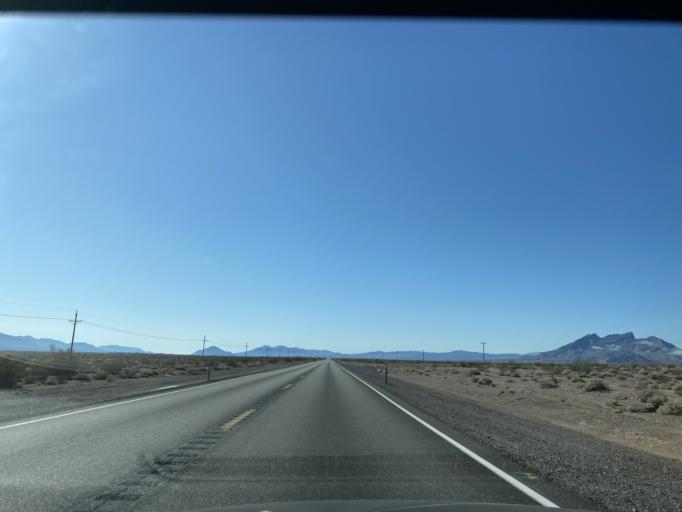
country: US
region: Nevada
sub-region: Nye County
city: Pahrump
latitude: 36.4652
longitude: -116.4217
